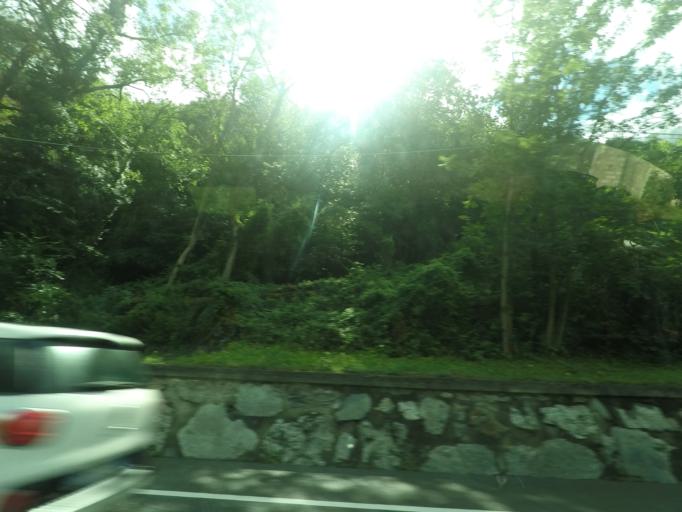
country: IT
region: Aosta Valley
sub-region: Valle d'Aosta
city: Chatillon
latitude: 45.7637
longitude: 7.6051
